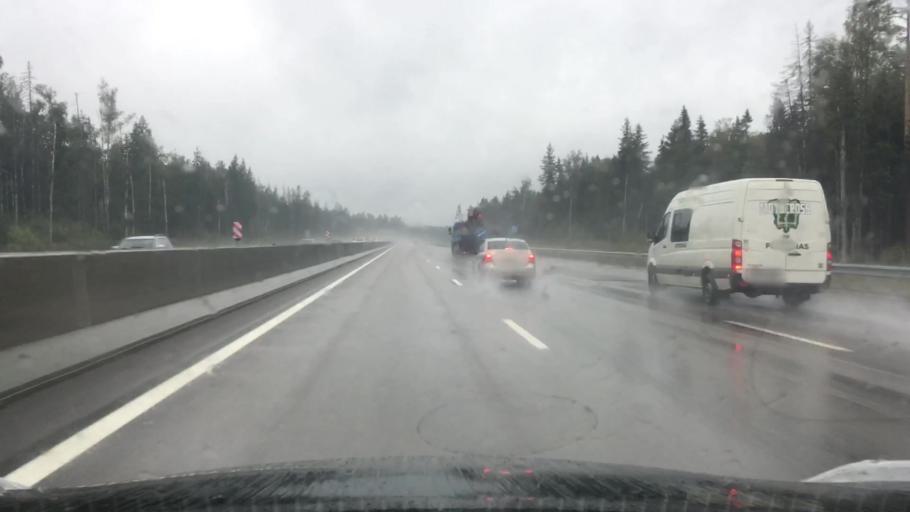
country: RU
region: Moskovskaya
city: Rzhavki
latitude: 56.0196
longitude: 37.2786
